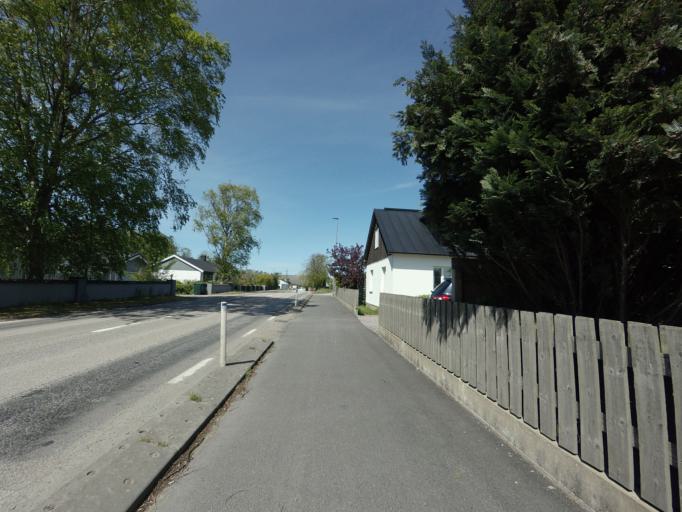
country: SE
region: Skane
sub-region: Helsingborg
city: Odakra
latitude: 56.1199
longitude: 12.6932
